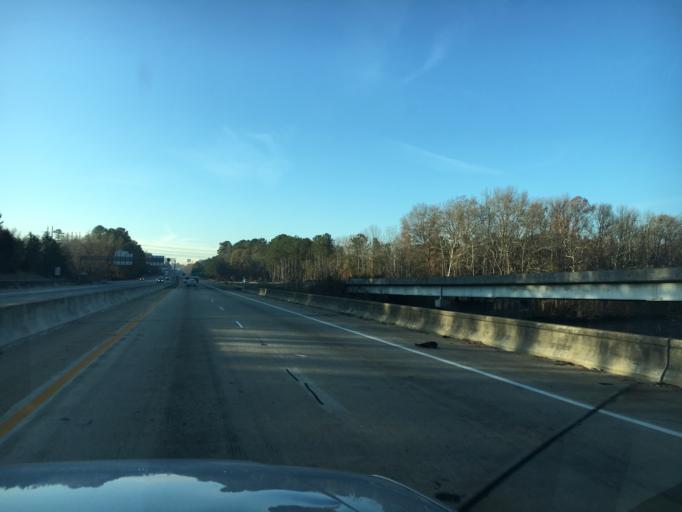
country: US
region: South Carolina
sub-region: Lexington County
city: Saint Andrews
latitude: 34.0238
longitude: -81.1036
